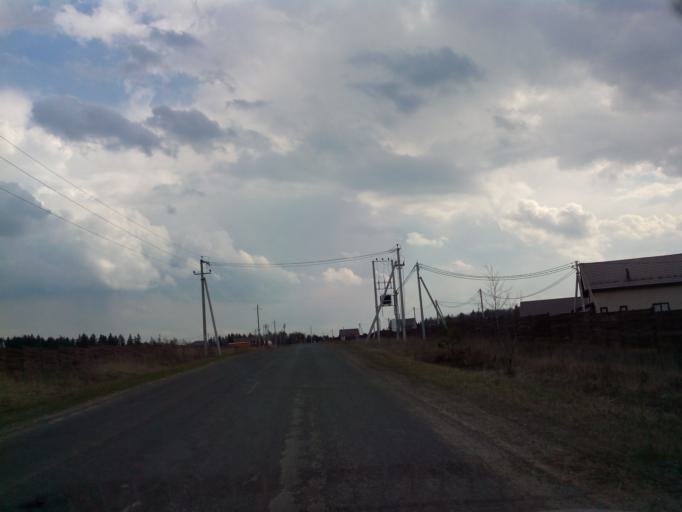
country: RU
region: Moskovskaya
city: Ruza
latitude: 55.5315
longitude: 36.2067
